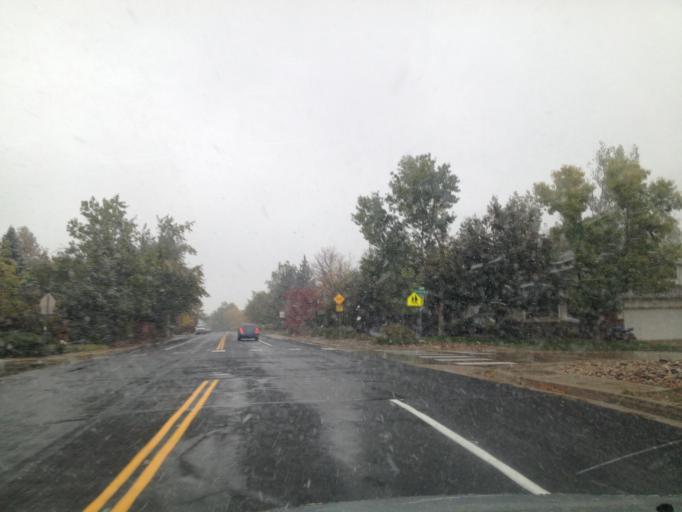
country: US
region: Colorado
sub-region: Boulder County
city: Louisville
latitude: 39.9827
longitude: -105.1542
